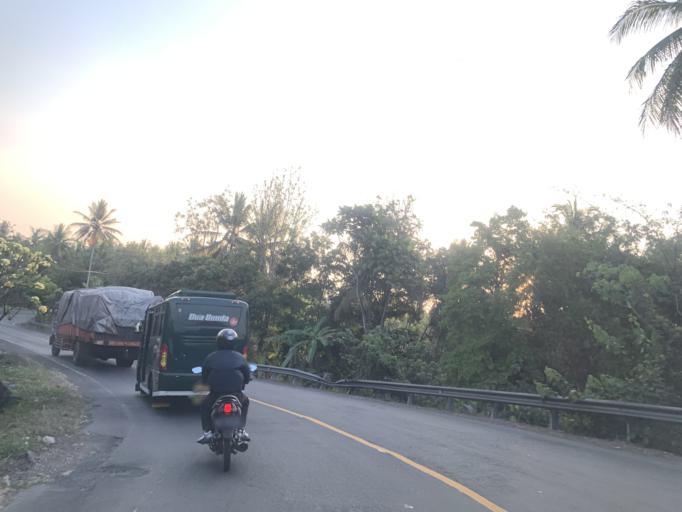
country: ID
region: Bali
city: Banjar Swastika
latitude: -8.4327
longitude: 114.8568
